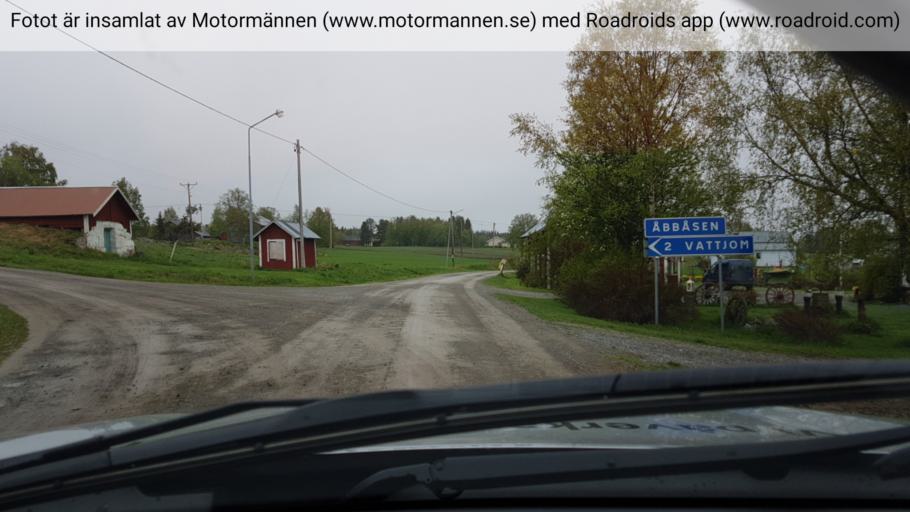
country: SE
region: Jaemtland
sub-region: Bergs Kommun
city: Hoverberg
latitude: 63.0203
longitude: 14.3775
